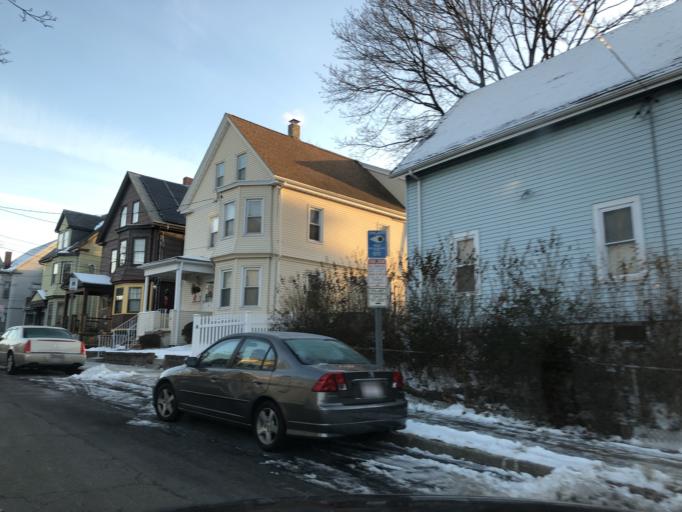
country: US
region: Massachusetts
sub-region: Middlesex County
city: Somerville
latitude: 42.3918
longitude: -71.1027
